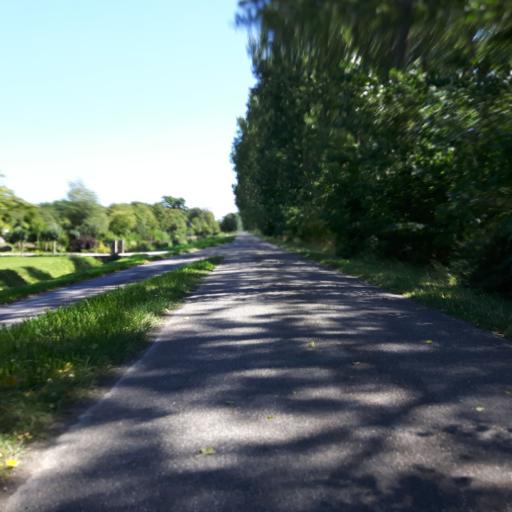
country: NL
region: Zeeland
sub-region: Gemeente Goes
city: Goes
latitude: 51.5634
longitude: 3.8196
